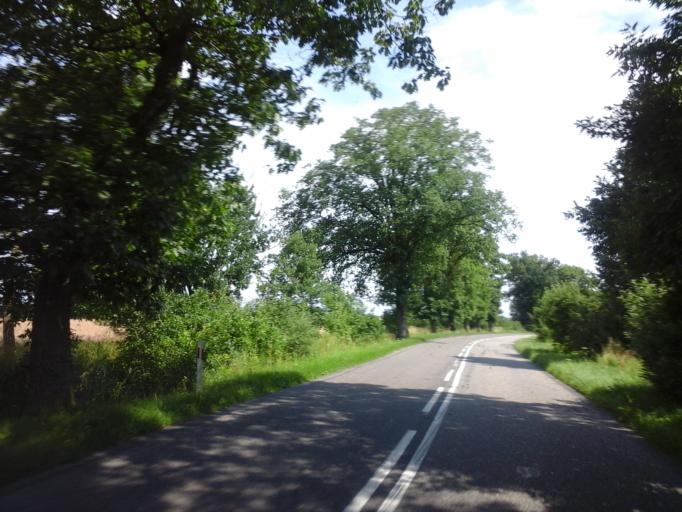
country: PL
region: West Pomeranian Voivodeship
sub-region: Powiat choszczenski
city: Recz
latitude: 53.3167
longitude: 15.5654
